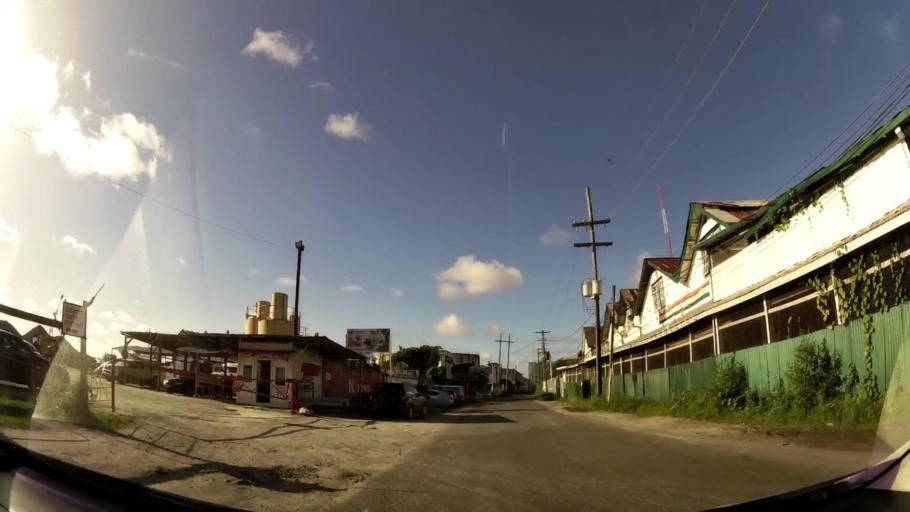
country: GY
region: Demerara-Mahaica
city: Georgetown
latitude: 6.8202
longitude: -58.1656
